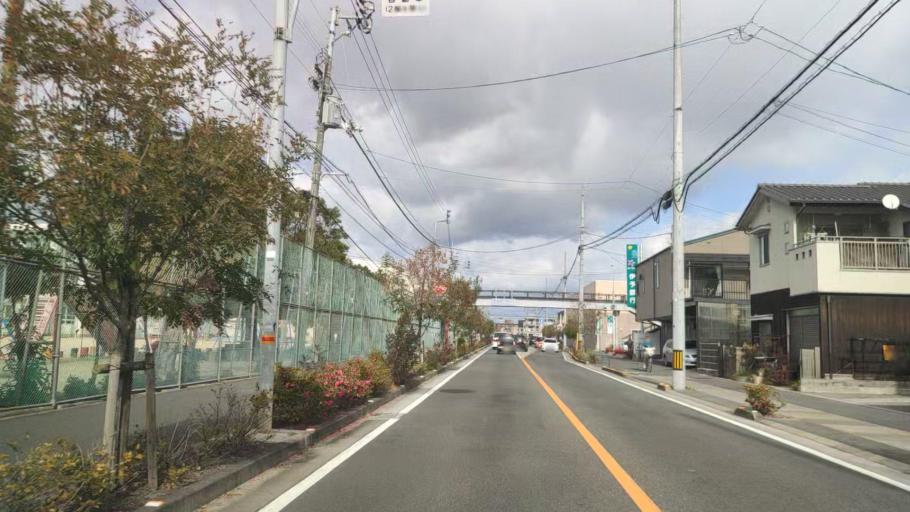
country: JP
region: Ehime
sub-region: Shikoku-chuo Shi
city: Matsuyama
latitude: 33.8103
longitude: 132.7608
